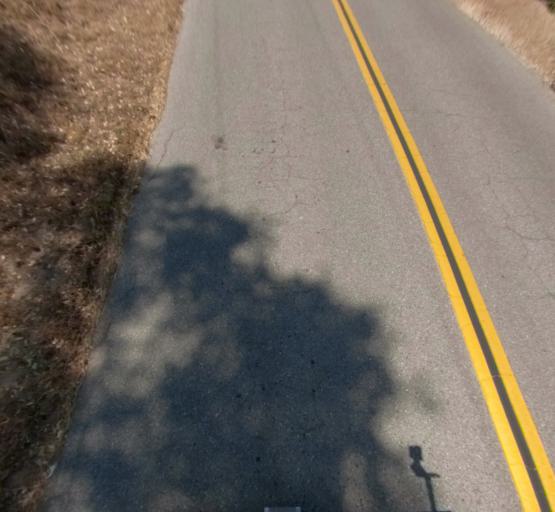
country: US
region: California
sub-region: Fresno County
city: Auberry
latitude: 37.2361
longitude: -119.4842
